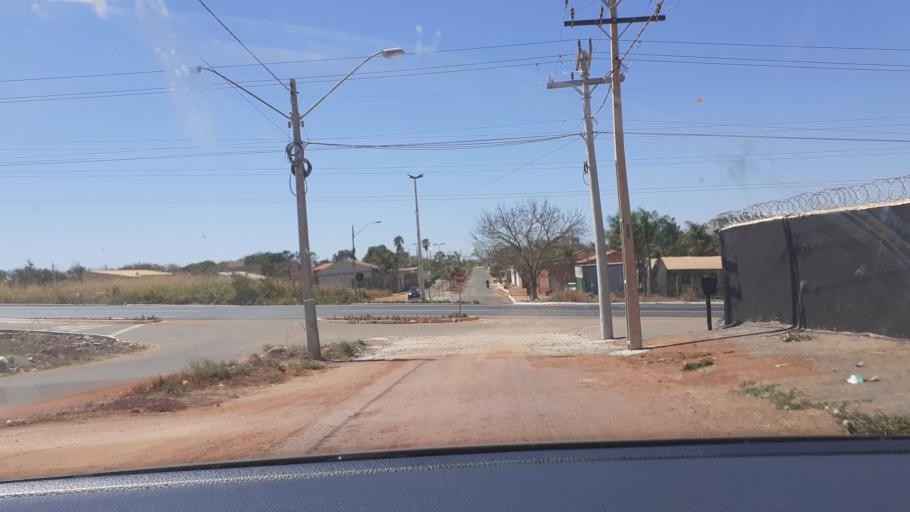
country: BR
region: Goias
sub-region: Caldas Novas
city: Caldas Novas
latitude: -17.7426
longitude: -48.6460
